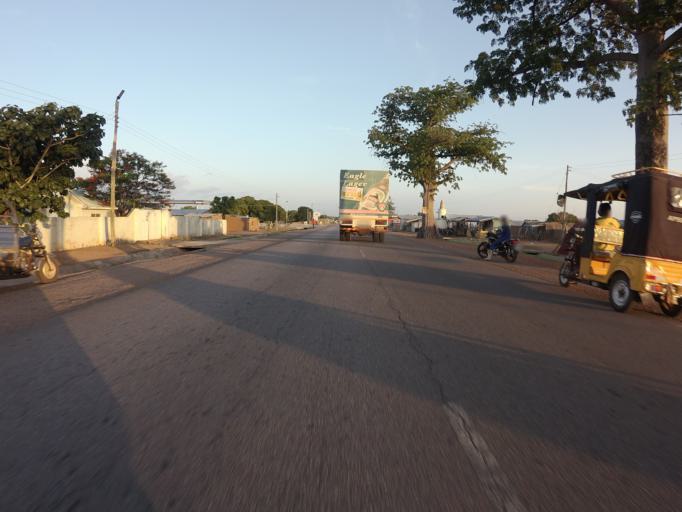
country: GH
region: Upper East
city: Navrongo
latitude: 10.9643
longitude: -1.1004
